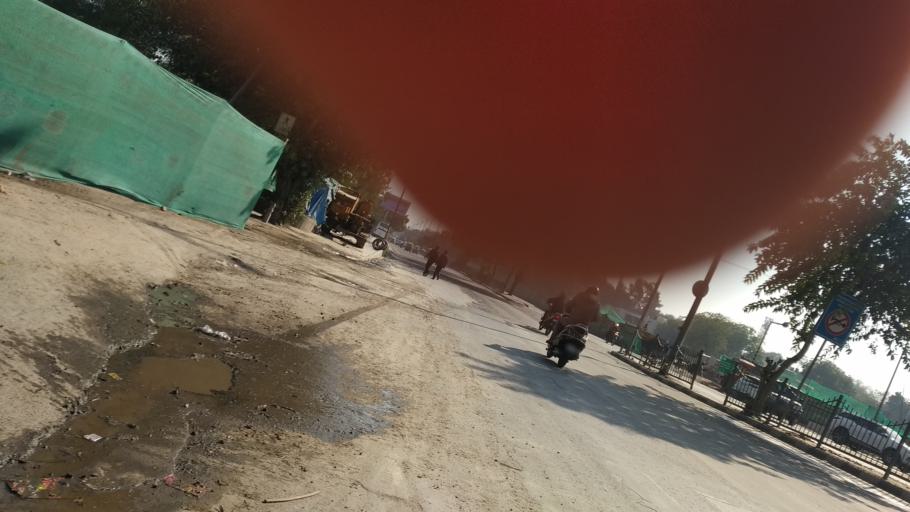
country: IN
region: NCT
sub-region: New Delhi
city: New Delhi
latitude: 28.6171
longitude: 77.2404
